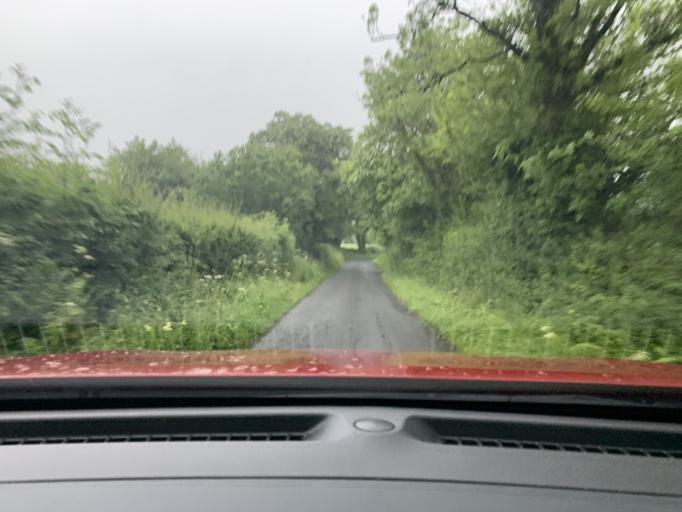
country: IE
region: Connaught
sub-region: Sligo
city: Sligo
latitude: 54.3216
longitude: -8.4490
